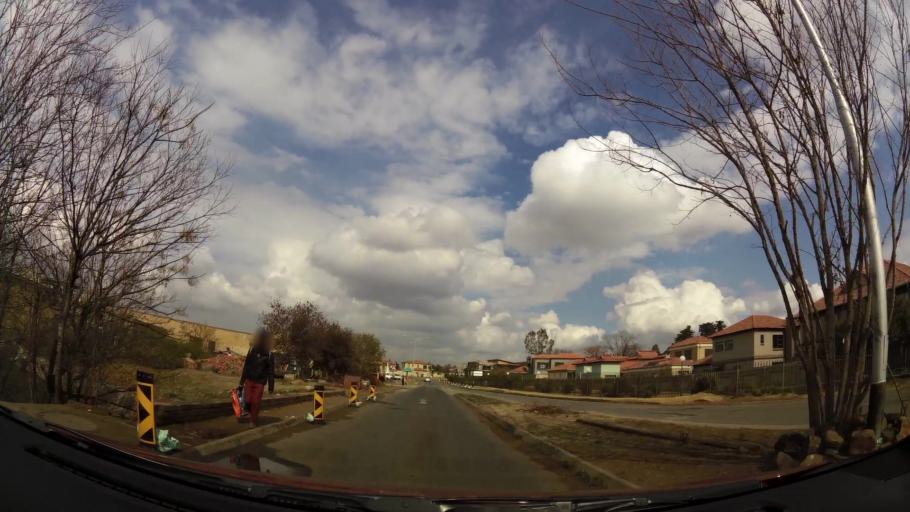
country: ZA
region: Gauteng
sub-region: Sedibeng District Municipality
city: Vanderbijlpark
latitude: -26.7340
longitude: 27.8376
